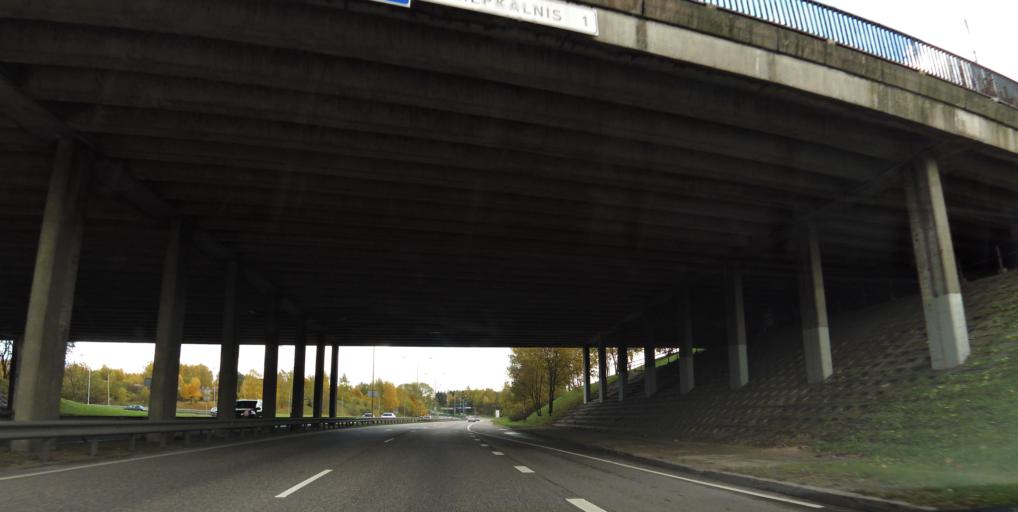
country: LT
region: Vilnius County
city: Naujamiestis
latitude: 54.6566
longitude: 25.2713
